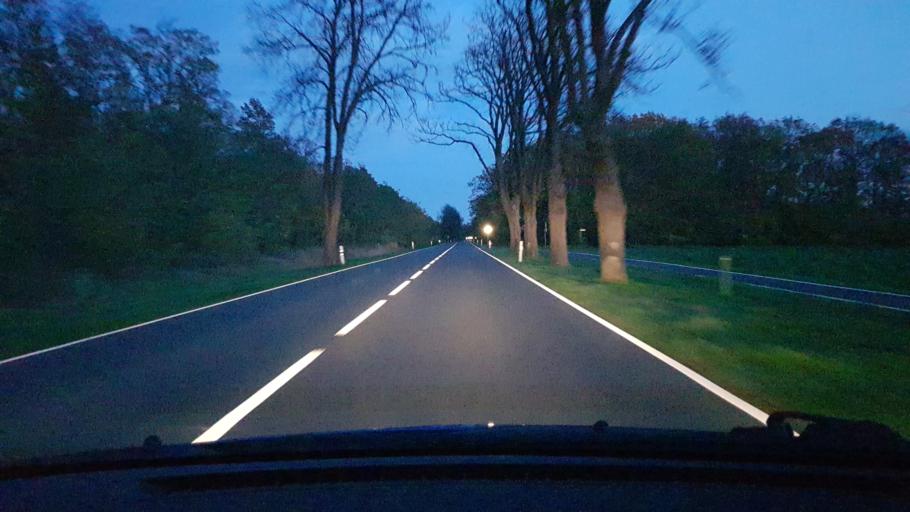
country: DE
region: Saxony-Anhalt
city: Rodleben
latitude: 51.9168
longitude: 12.1792
